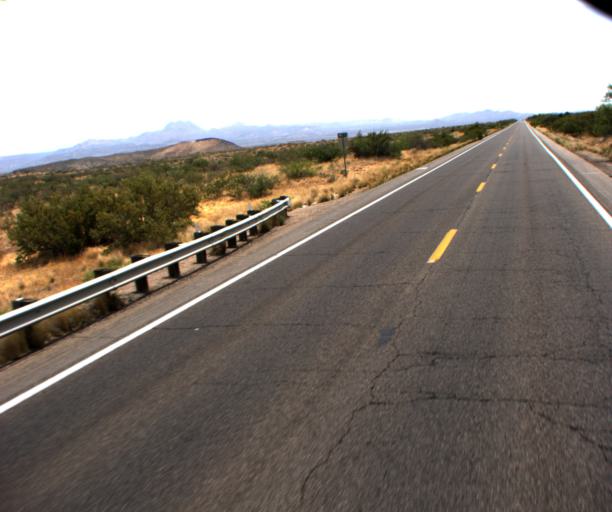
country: US
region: Arizona
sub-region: Gila County
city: Peridot
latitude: 33.3171
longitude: -110.5260
